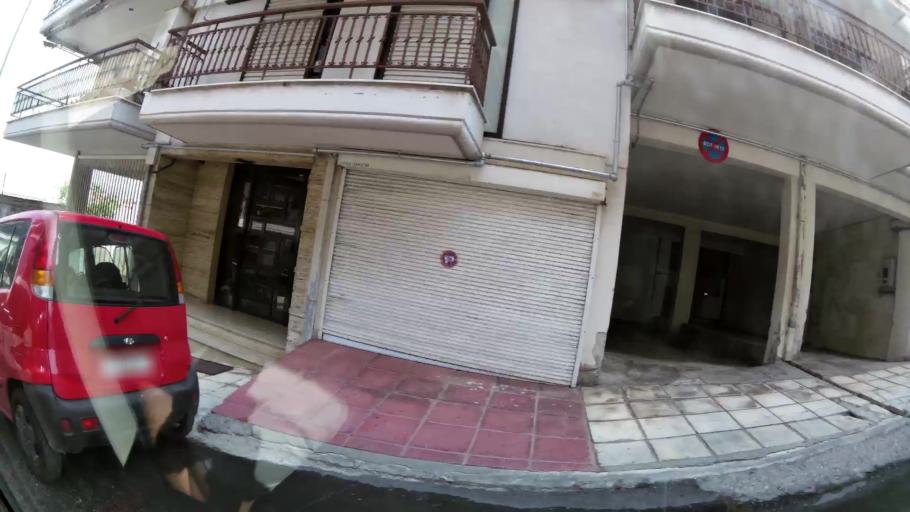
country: GR
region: Central Macedonia
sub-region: Nomos Thessalonikis
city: Thessaloniki
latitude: 40.6476
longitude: 22.9399
